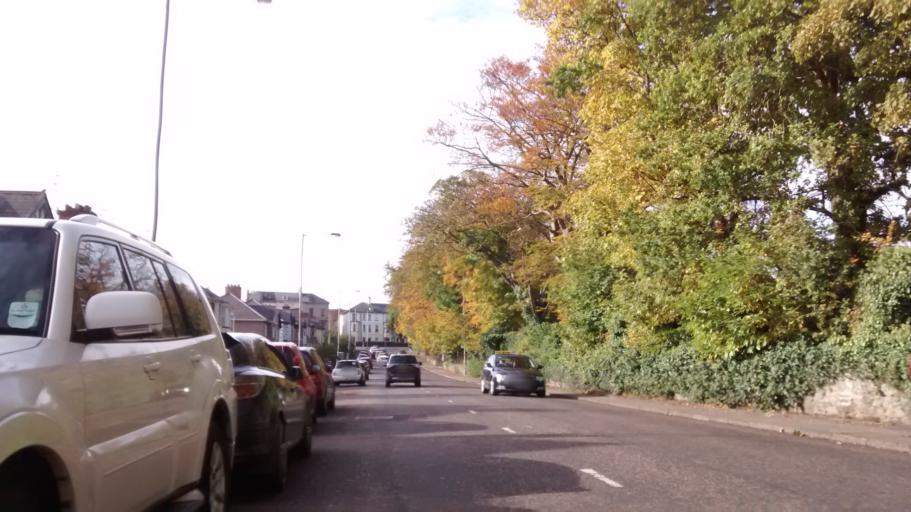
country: GB
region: Northern Ireland
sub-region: City of Derry
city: Derry
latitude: 55.0095
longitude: -7.3228
